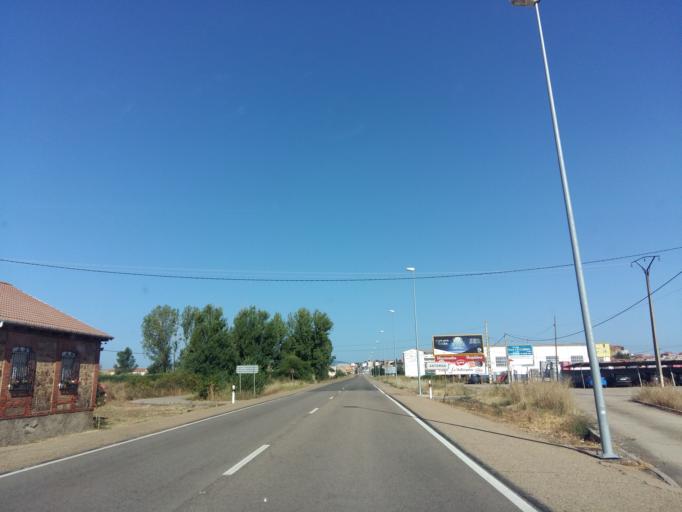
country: ES
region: Castille and Leon
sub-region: Provincia de Leon
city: Astorga
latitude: 42.4462
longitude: -6.0466
